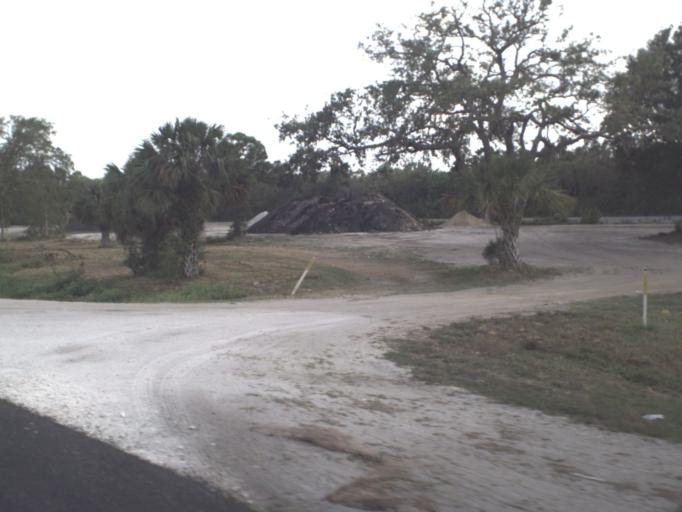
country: US
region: Florida
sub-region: Brevard County
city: Port Saint John
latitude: 28.5363
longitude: -80.7924
